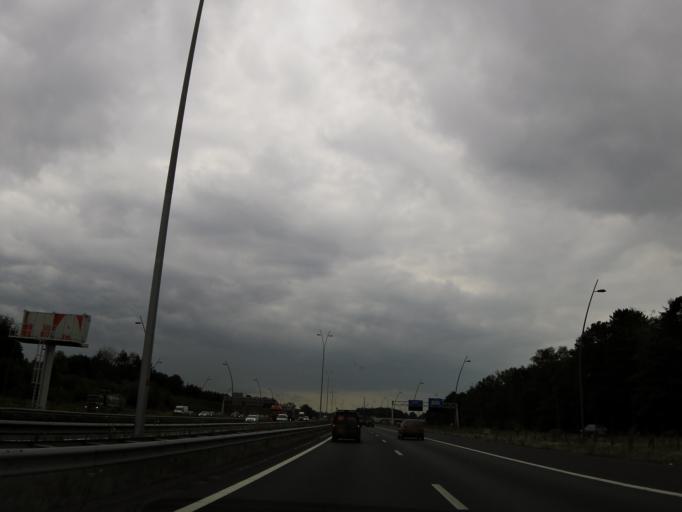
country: NL
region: North Brabant
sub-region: Gemeente Eindhoven
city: Meerhoven
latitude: 51.4533
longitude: 5.4181
